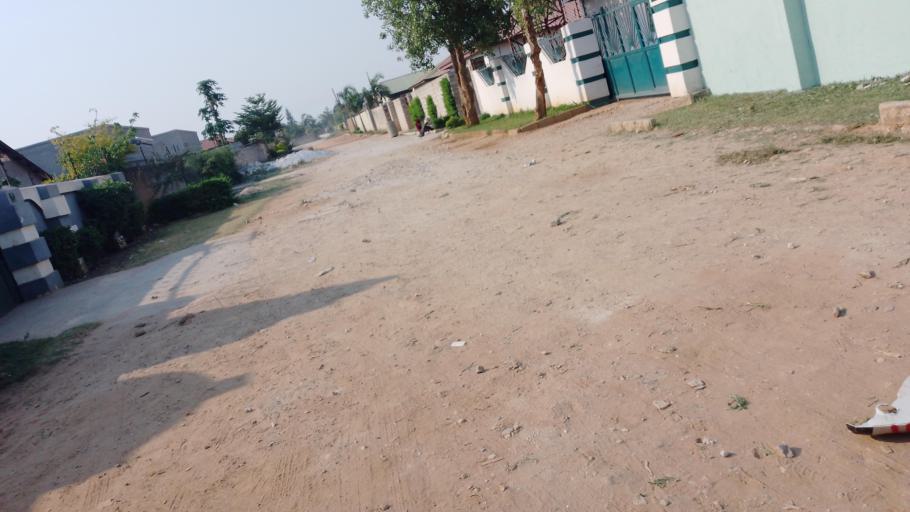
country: ZM
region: Lusaka
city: Lusaka
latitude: -15.3980
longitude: 28.3858
